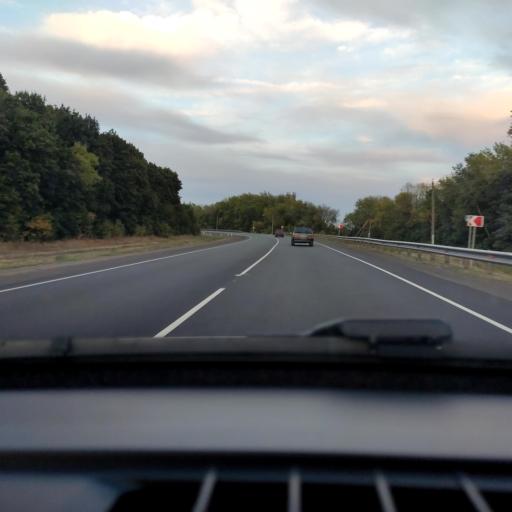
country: RU
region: Voronezj
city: Panino
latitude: 51.4900
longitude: 40.2341
